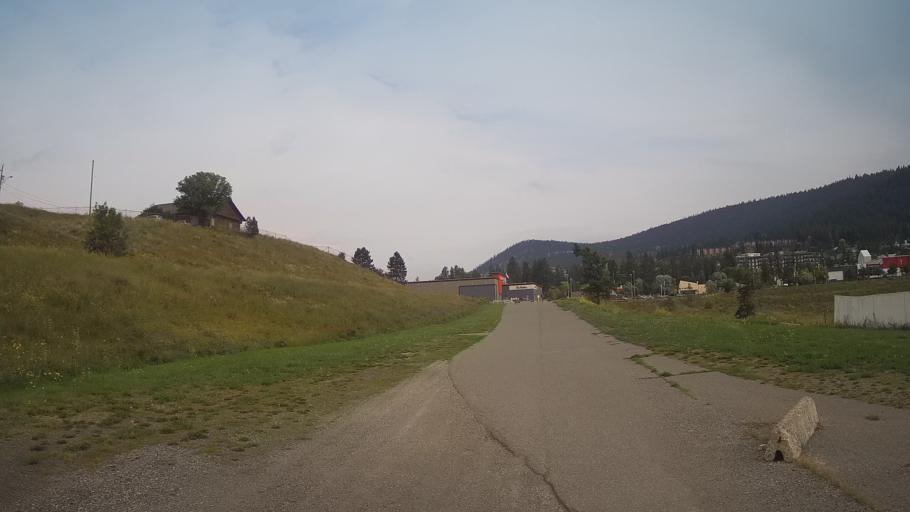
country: CA
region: British Columbia
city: Williams Lake
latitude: 52.1260
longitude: -122.1339
